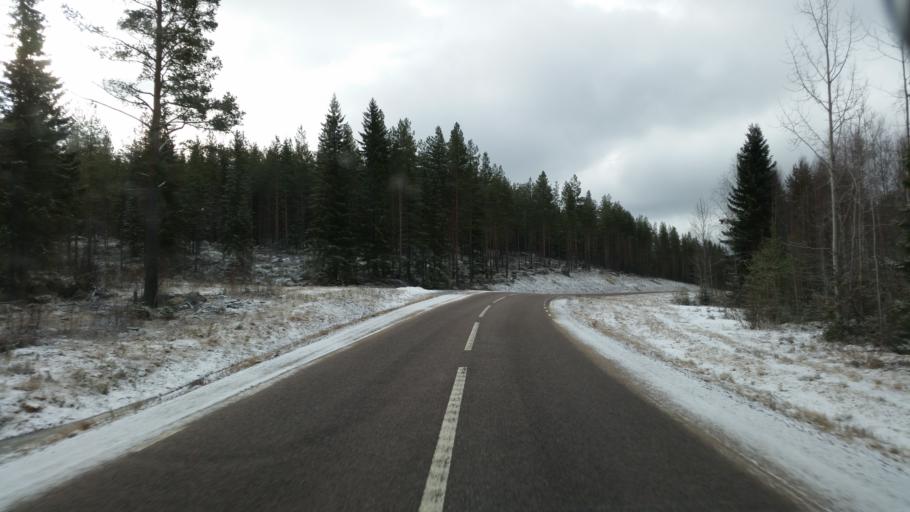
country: SE
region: Gaevleborg
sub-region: Ovanakers Kommun
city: Edsbyn
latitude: 61.5678
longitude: 15.6726
